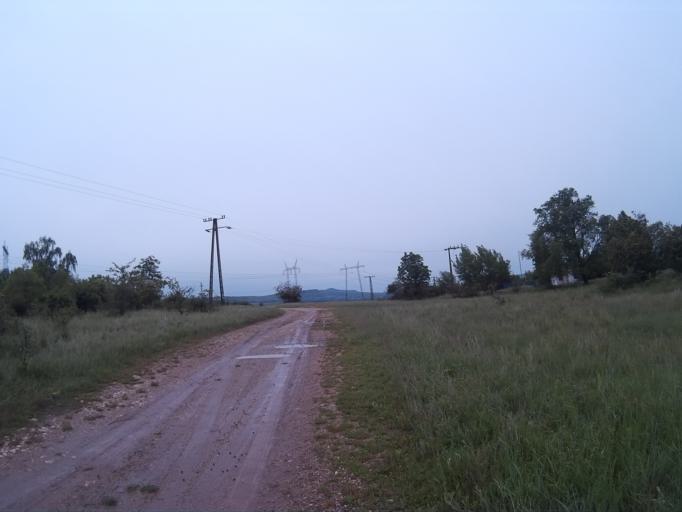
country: HU
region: Veszprem
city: Sumeg
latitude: 46.9647
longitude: 17.2929
